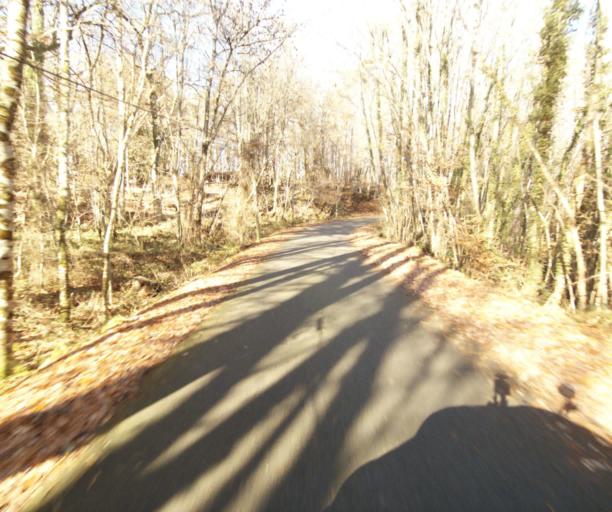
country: FR
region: Limousin
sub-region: Departement de la Correze
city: Sainte-Fortunade
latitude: 45.2106
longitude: 1.7820
